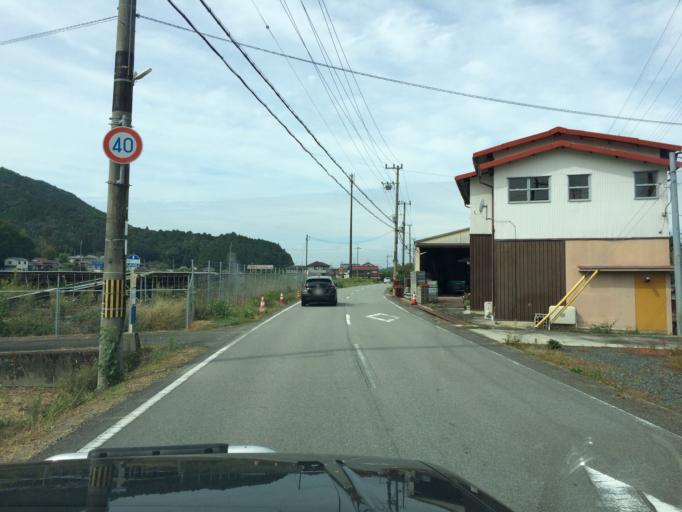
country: JP
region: Hyogo
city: Sasayama
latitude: 35.0688
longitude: 135.2722
